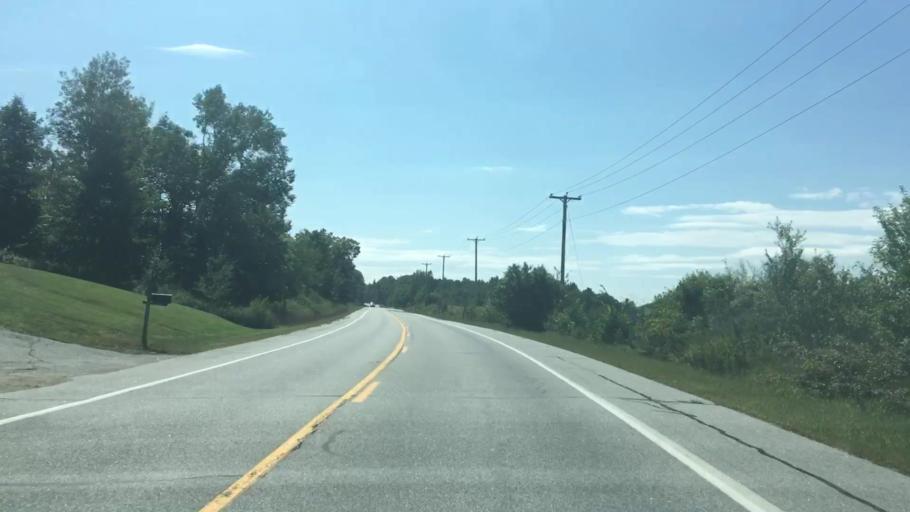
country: US
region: Maine
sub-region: Kennebec County
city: Monmouth
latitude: 44.1643
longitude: -70.0289
